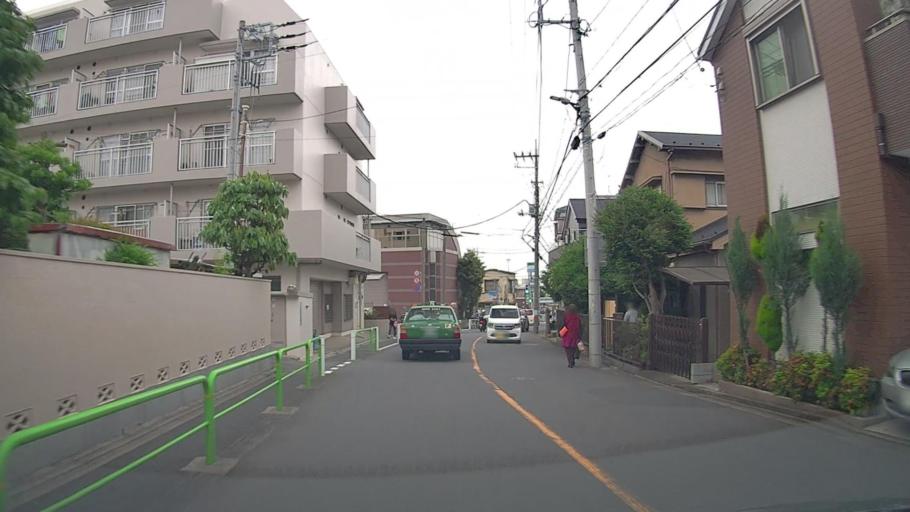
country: JP
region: Saitama
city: Shimotoda
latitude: 35.7704
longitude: 139.6759
